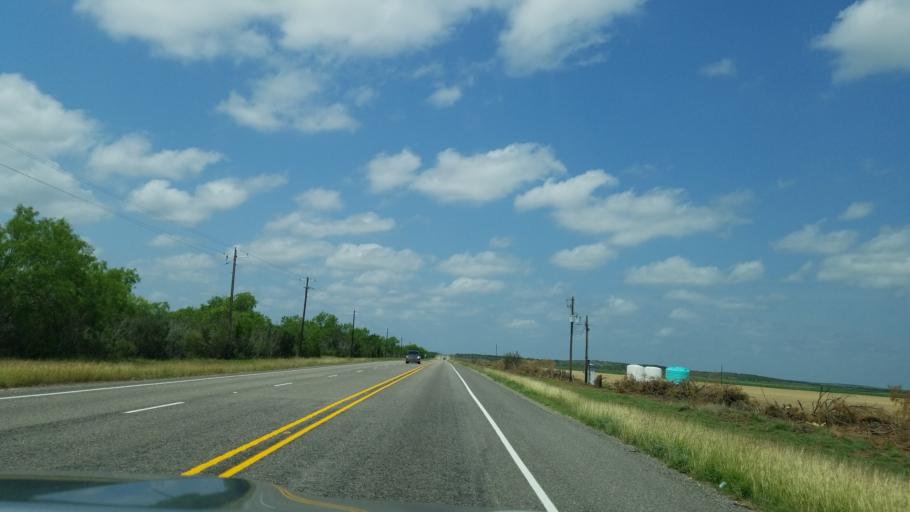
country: US
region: Texas
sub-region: Frio County
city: Pearsall
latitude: 28.9459
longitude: -99.2824
